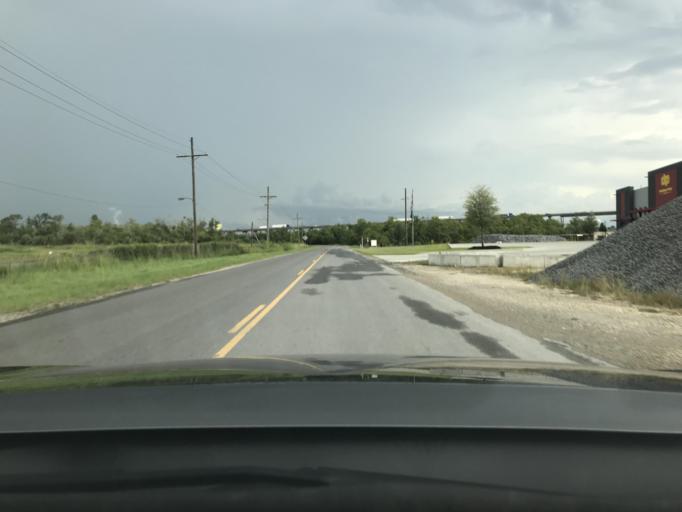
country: US
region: Louisiana
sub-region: Calcasieu Parish
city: Westlake
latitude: 30.2314
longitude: -93.2524
